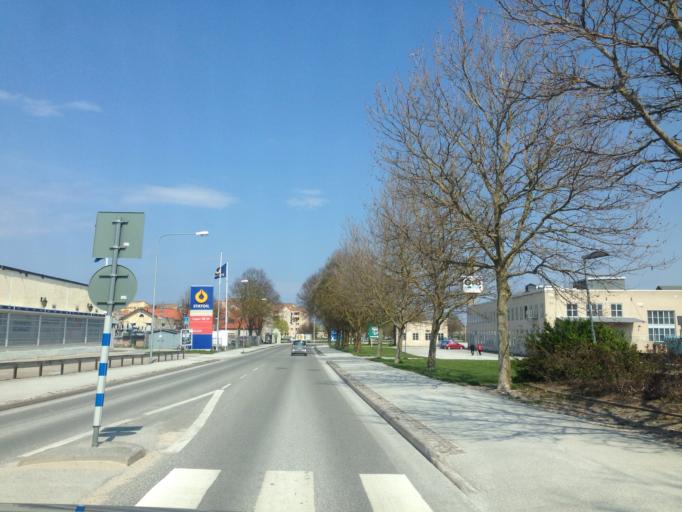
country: SE
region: Gotland
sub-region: Gotland
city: Visby
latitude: 57.6292
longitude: 18.2878
